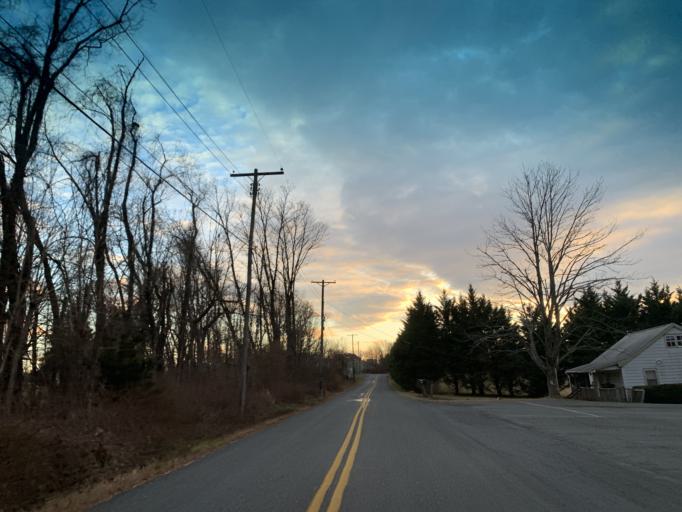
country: US
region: Maryland
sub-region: Harford County
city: South Bel Air
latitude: 39.5956
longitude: -76.3221
